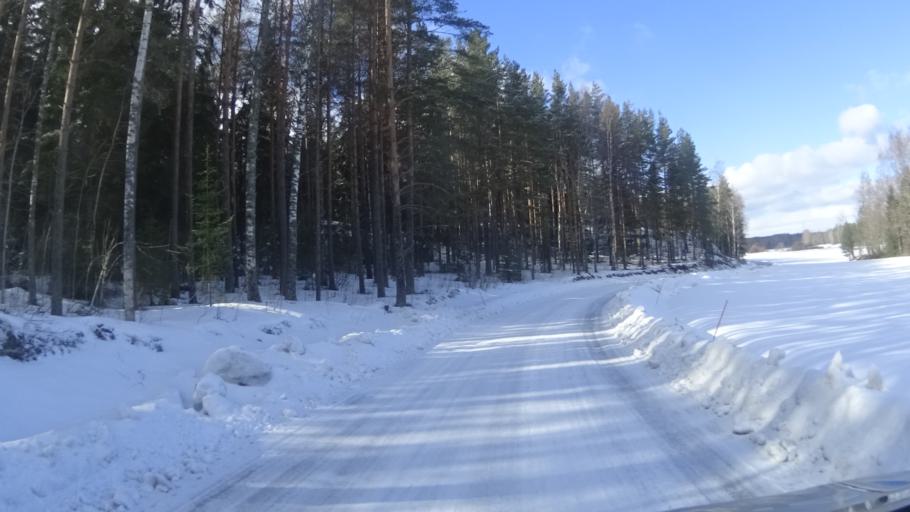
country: FI
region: Uusimaa
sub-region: Helsinki
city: Vantaa
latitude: 60.2396
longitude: 25.1814
